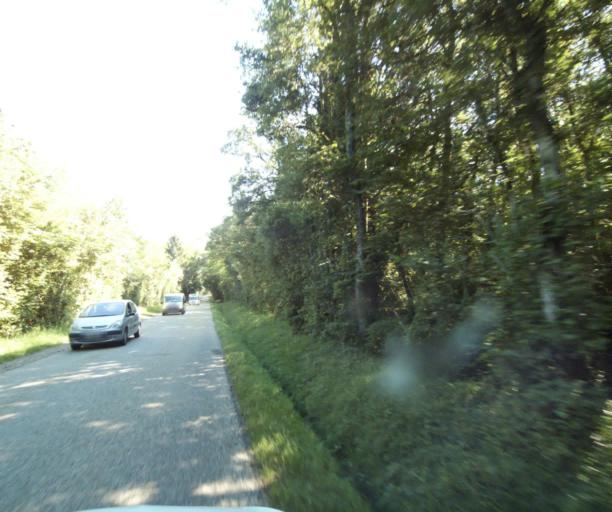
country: FR
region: Rhone-Alpes
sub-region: Departement de la Haute-Savoie
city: Ballaison
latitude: 46.2876
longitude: 6.3475
